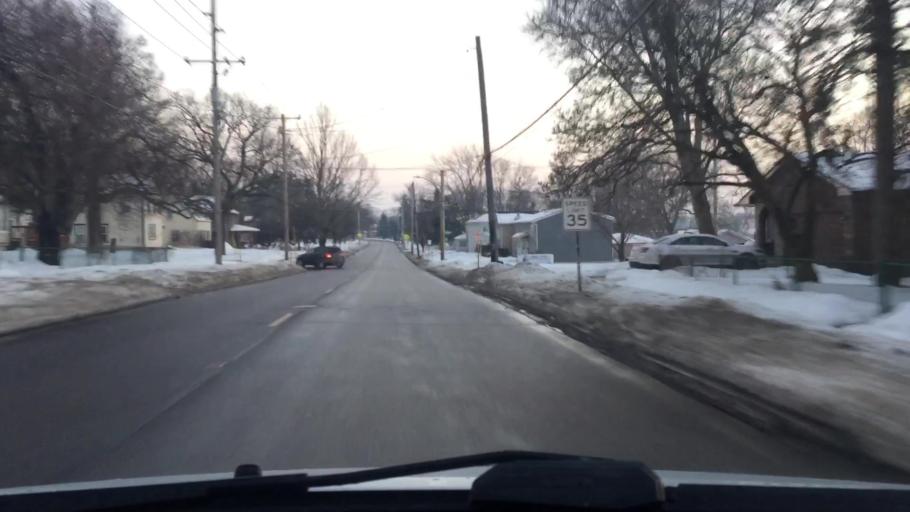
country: US
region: Illinois
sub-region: Kane County
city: Batavia
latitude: 41.8601
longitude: -88.3065
